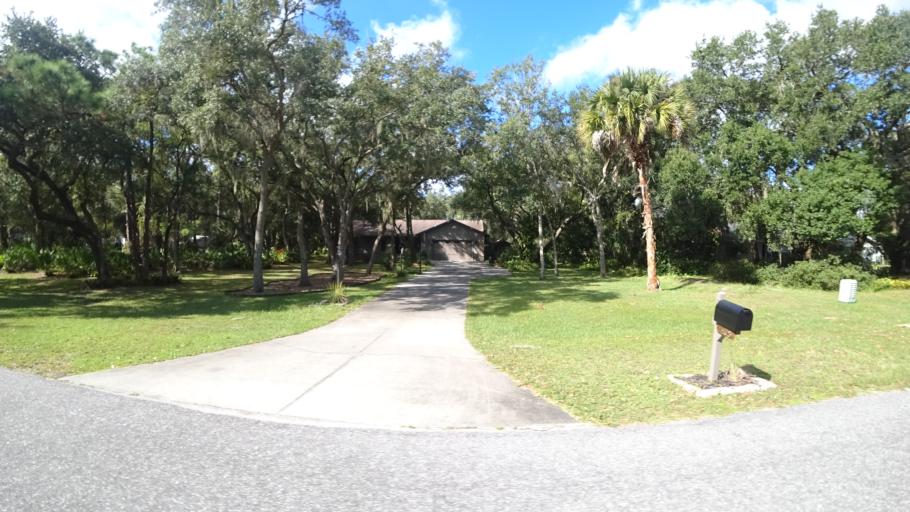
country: US
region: Florida
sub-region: Sarasota County
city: North Sarasota
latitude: 27.4083
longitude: -82.5041
